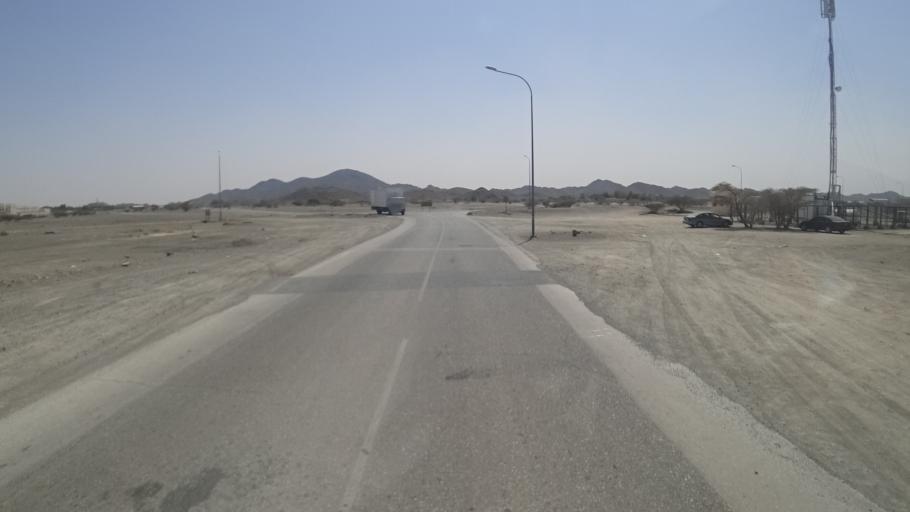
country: OM
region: Ash Sharqiyah
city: Ibra'
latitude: 22.6524
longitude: 58.5250
